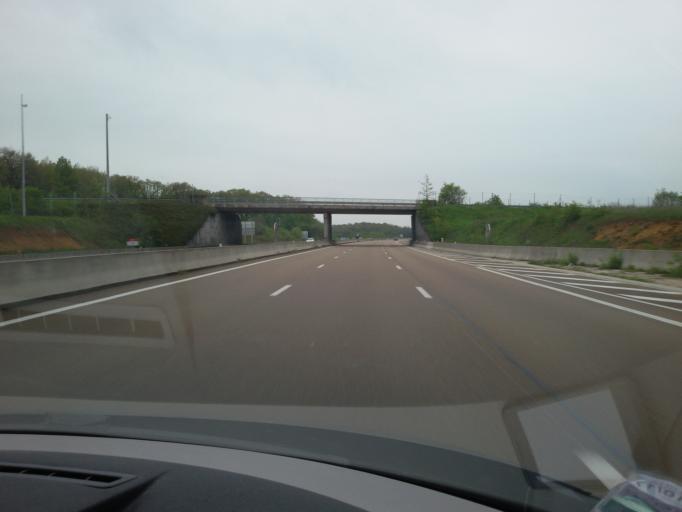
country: FR
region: Bourgogne
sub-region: Departement de la Cote-d'Or
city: Saint-Julien
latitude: 47.4290
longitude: 5.1696
